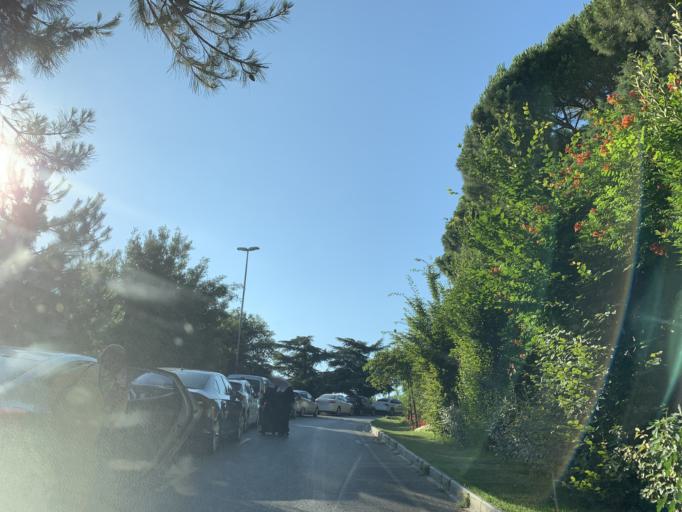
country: TR
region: Istanbul
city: Pendik
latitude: 40.8901
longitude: 29.2529
